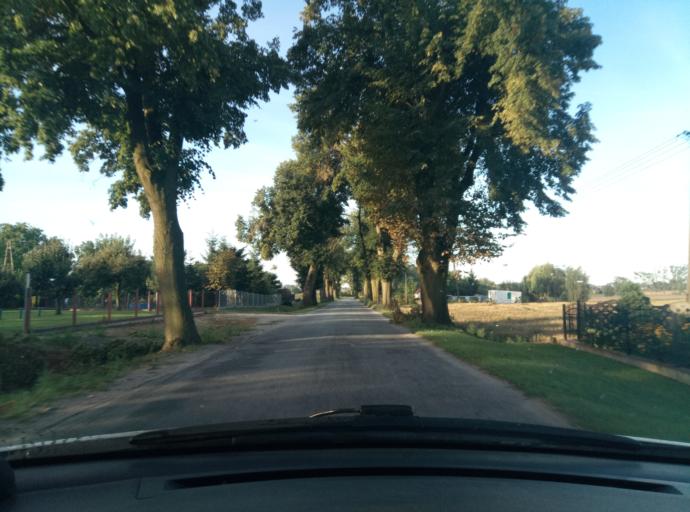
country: PL
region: Kujawsko-Pomorskie
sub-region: Powiat brodnicki
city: Jablonowo Pomorskie
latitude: 53.4093
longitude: 19.1742
